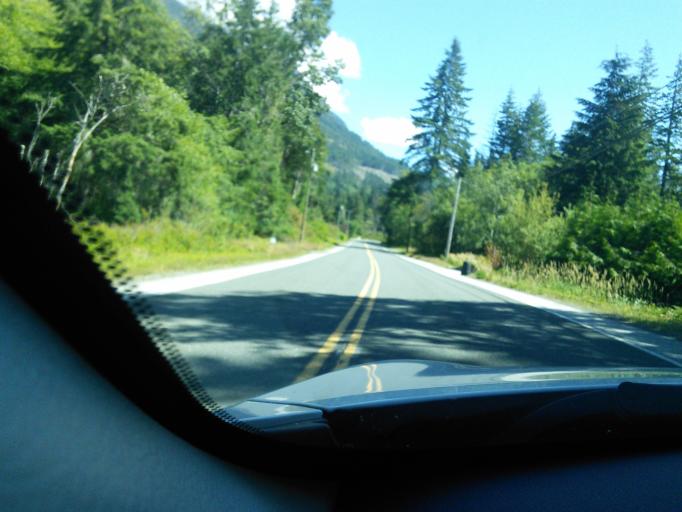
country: CA
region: British Columbia
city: Campbell River
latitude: 50.3553
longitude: -125.9118
